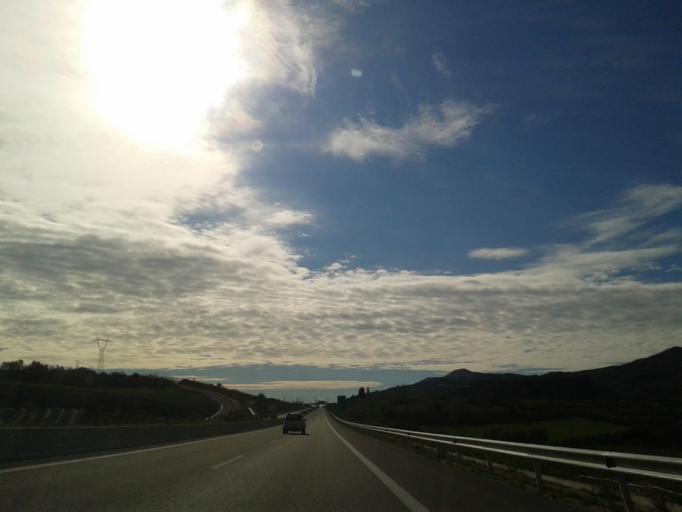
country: GR
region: West Greece
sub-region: Nomos Aitolias kai Akarnanias
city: Fitiai
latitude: 38.7104
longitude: 21.2091
